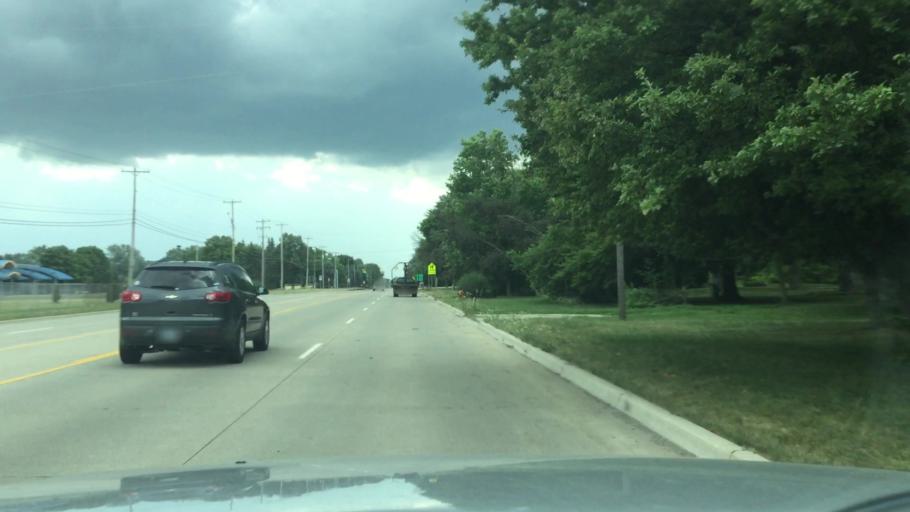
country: US
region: Michigan
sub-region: Genesee County
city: Flushing
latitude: 43.0270
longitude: -83.7735
